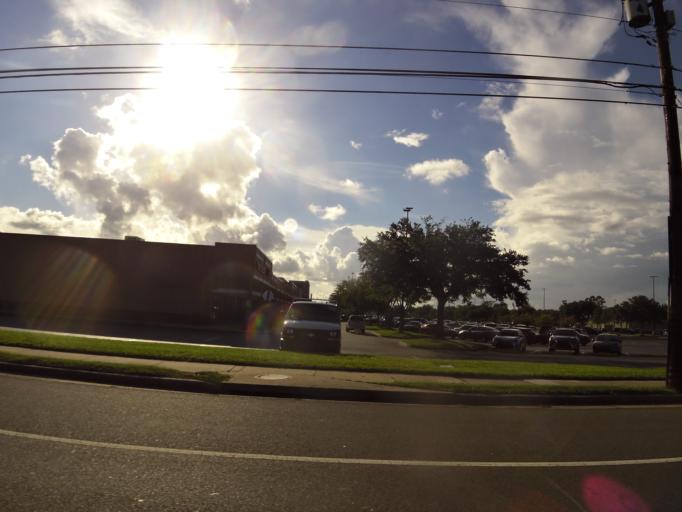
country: US
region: Georgia
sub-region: Glynn County
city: Country Club Estates
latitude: 31.2133
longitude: -81.4808
